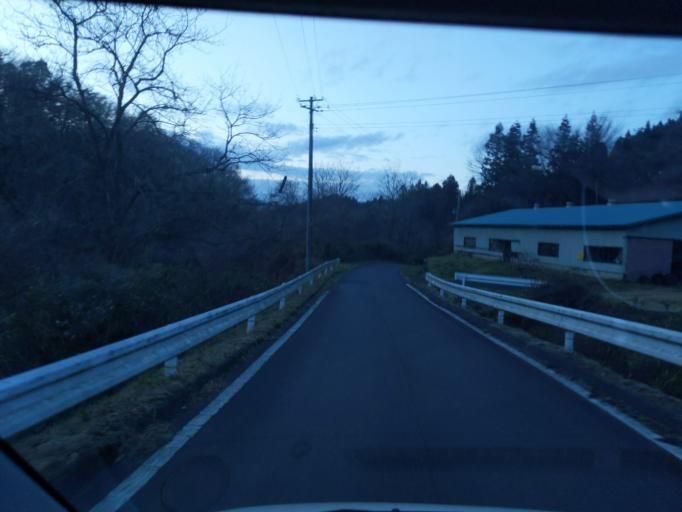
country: JP
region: Iwate
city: Ichinoseki
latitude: 38.8317
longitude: 141.0888
